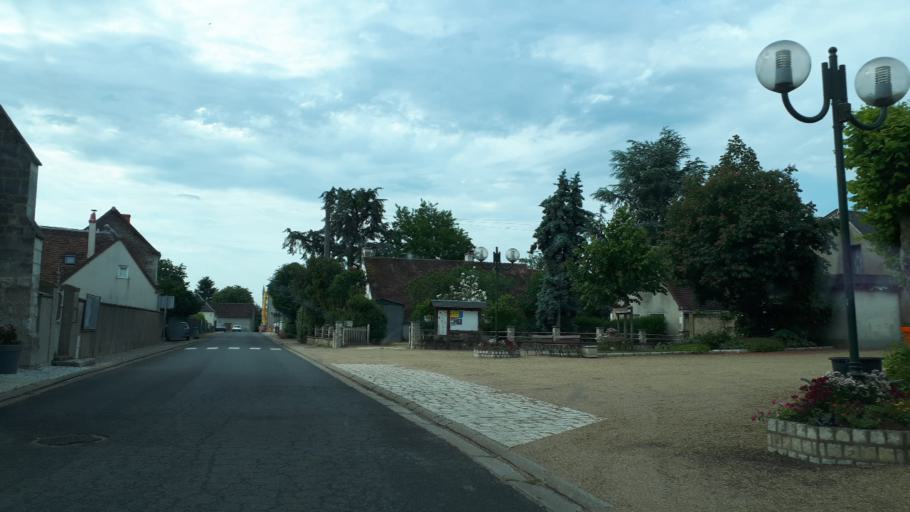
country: FR
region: Centre
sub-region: Departement du Loir-et-Cher
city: Saint-Amand-Longpre
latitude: 47.7234
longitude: 1.0092
